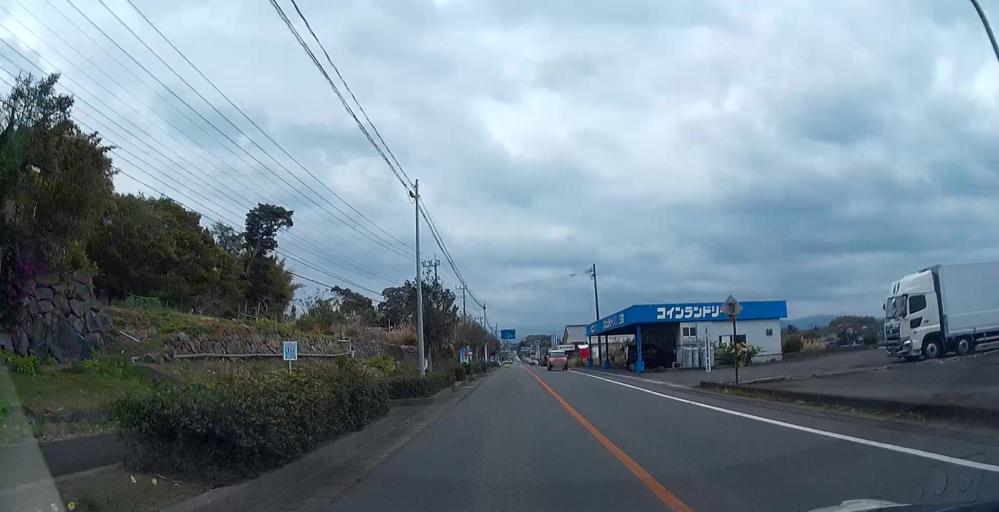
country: JP
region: Kagoshima
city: Akune
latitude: 32.0844
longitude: 130.1968
